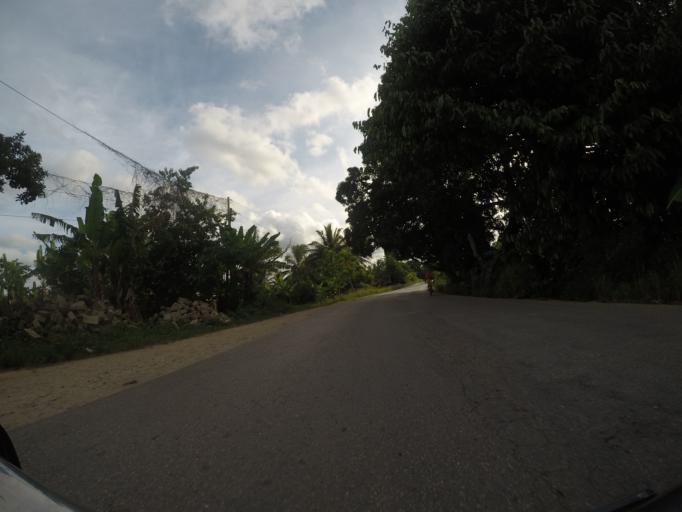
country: TZ
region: Pemba South
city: Chake Chake
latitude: -5.2806
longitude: 39.7665
